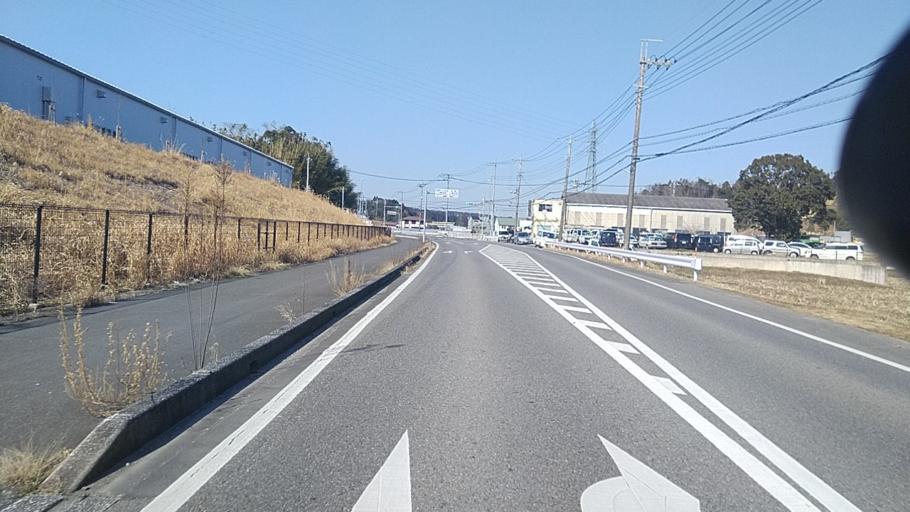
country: JP
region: Chiba
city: Mobara
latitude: 35.4701
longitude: 140.2824
